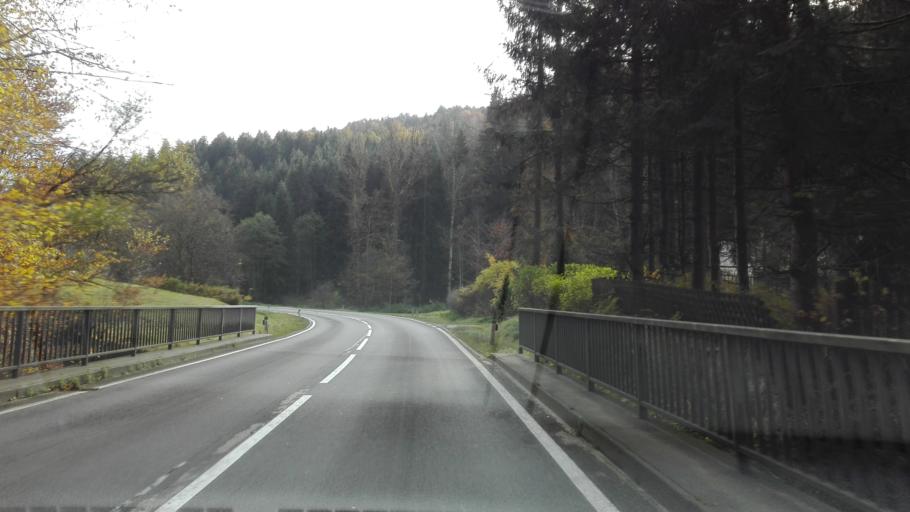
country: AT
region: Upper Austria
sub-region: Politischer Bezirk Rohrbach
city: Atzesberg
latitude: 48.4135
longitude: 13.8811
